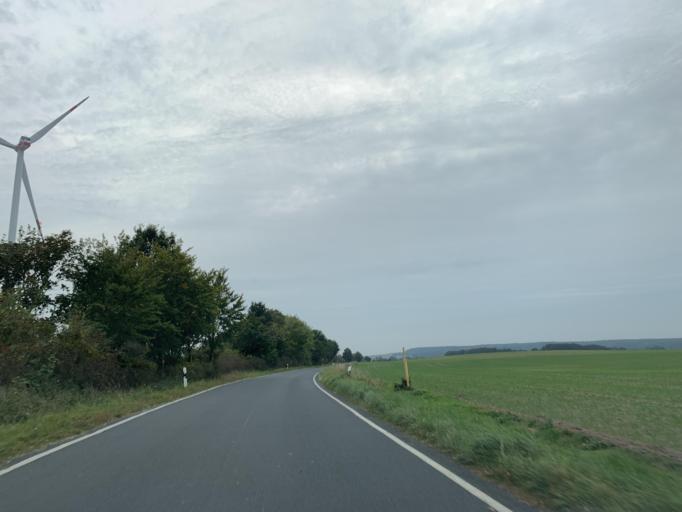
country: DE
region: Brandenburg
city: Mittenwalde
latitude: 53.3211
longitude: 13.6986
